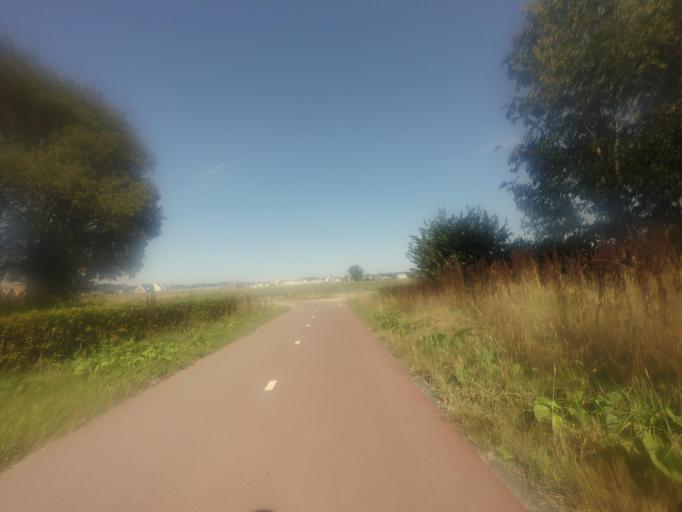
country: NL
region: North Brabant
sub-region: Gemeente Veldhoven
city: Oerle
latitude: 51.4044
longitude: 5.3792
